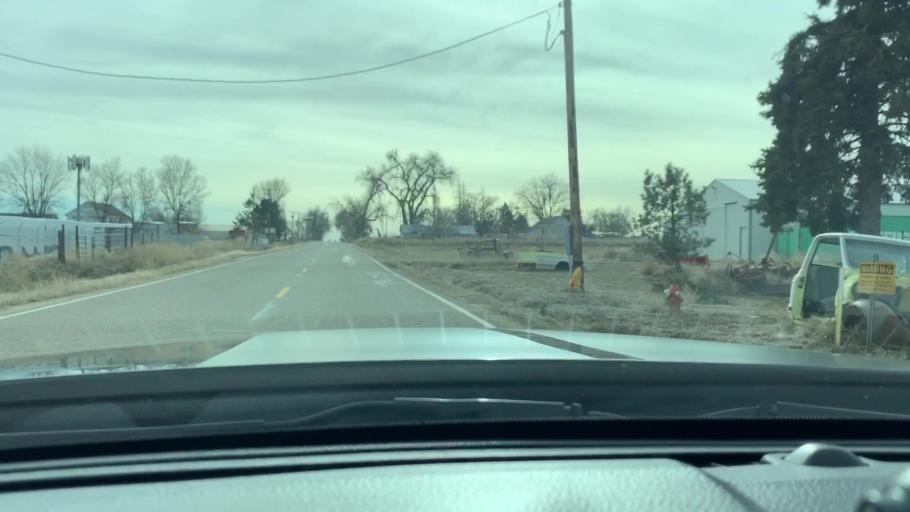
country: US
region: Colorado
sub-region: Weld County
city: Johnstown
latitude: 40.3551
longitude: -104.9835
